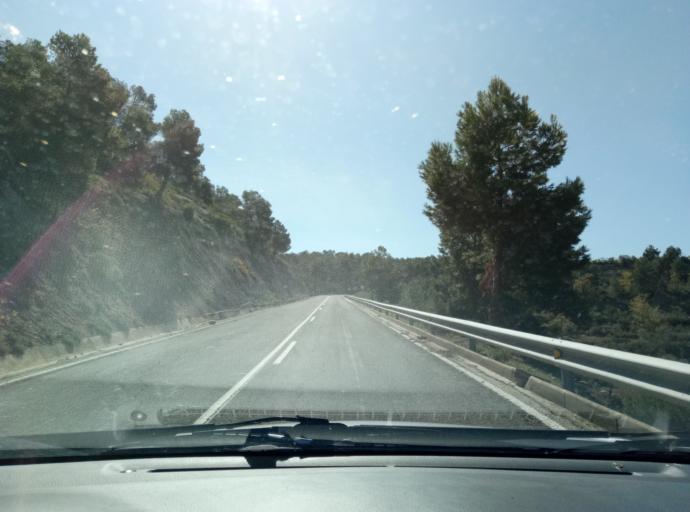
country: ES
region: Catalonia
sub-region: Provincia de Lleida
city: Vallbona de les Monges
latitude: 41.5310
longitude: 1.0252
